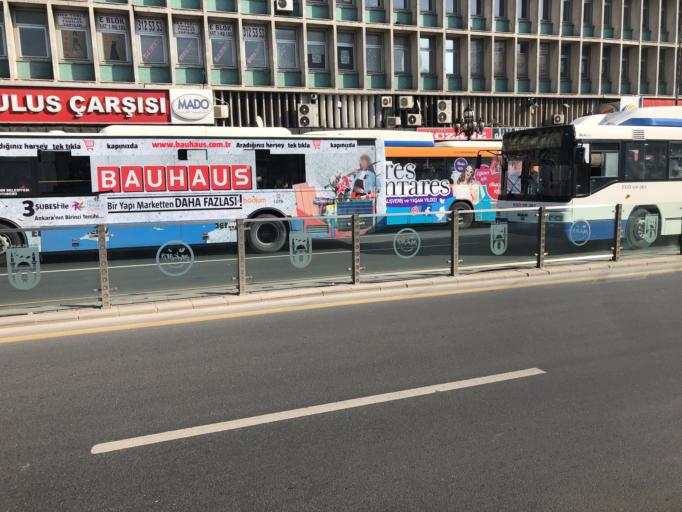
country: TR
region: Ankara
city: Ankara
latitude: 39.9412
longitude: 32.8543
